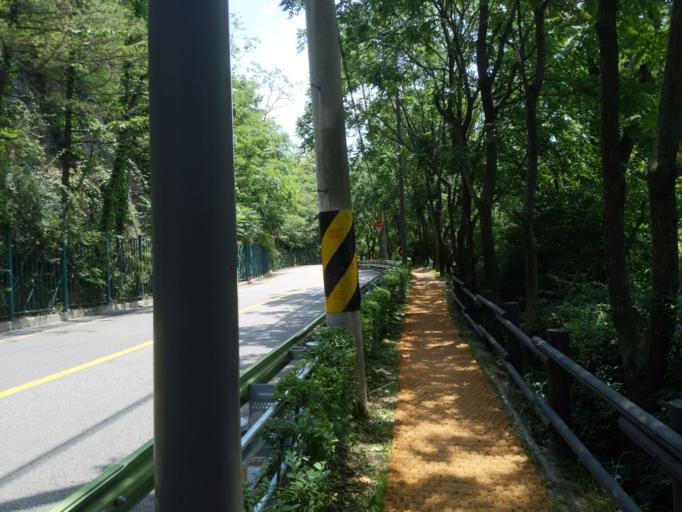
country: KR
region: Seoul
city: Seoul
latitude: 37.5994
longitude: 126.9729
